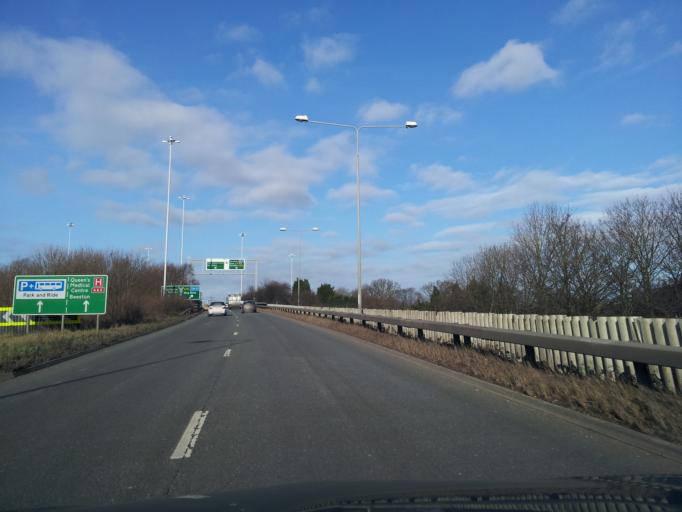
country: GB
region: England
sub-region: Nottinghamshire
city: Ruddington
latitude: 52.9206
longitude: -1.1628
